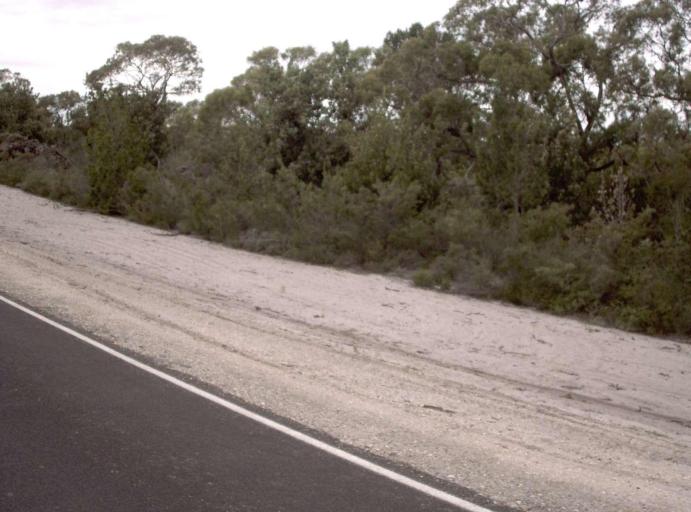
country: AU
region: Victoria
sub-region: Wellington
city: Sale
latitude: -38.1770
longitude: 147.3801
